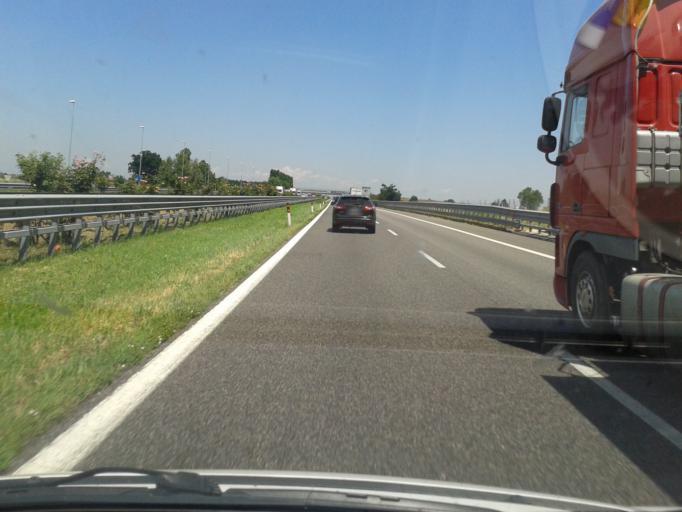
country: IT
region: Lombardy
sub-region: Provincia di Cremona
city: Battaglione-Bagnara
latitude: 45.1196
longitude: 10.0611
